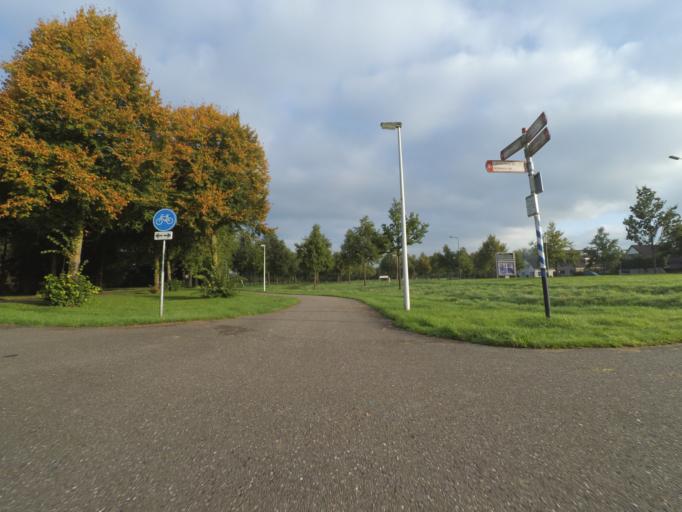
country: NL
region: Flevoland
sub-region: Gemeente Dronten
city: Dronten
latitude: 52.5180
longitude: 5.6901
